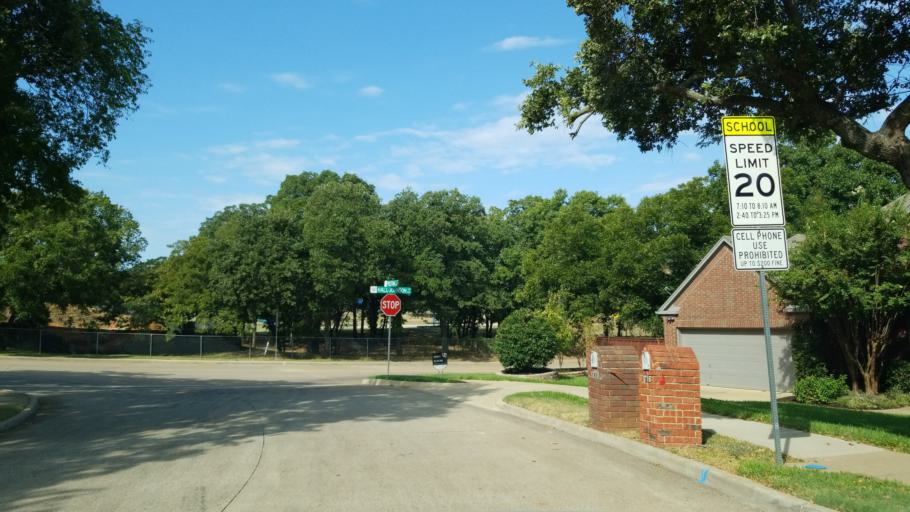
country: US
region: Texas
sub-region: Tarrant County
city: Grapevine
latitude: 32.8910
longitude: -97.0909
